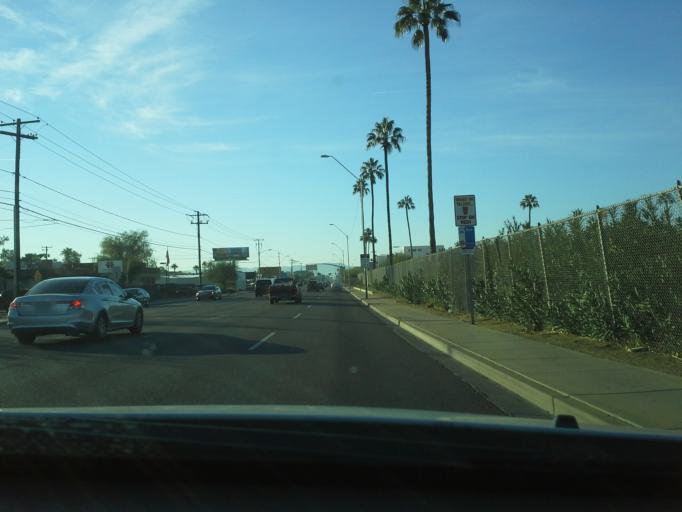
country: US
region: Arizona
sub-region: Maricopa County
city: Phoenix
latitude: 33.5018
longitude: -112.0651
